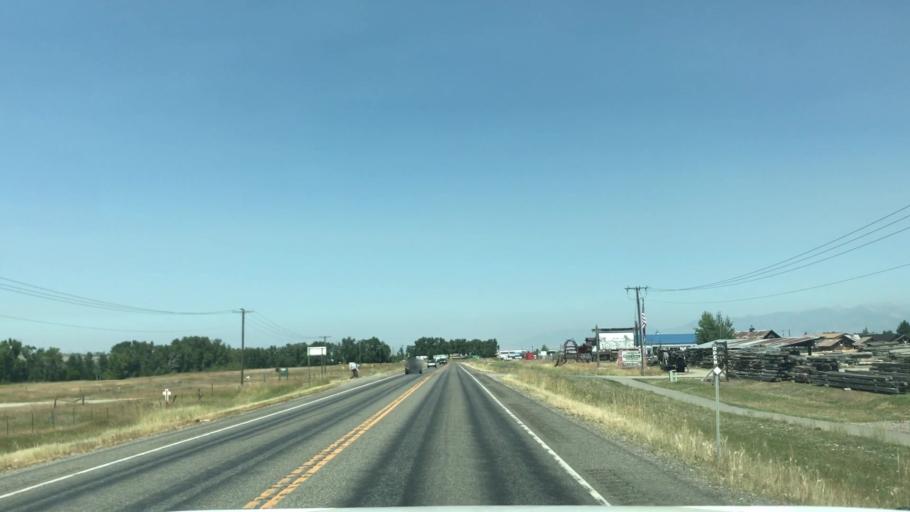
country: US
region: Montana
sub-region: Gallatin County
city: Four Corners
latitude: 45.6030
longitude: -111.1961
